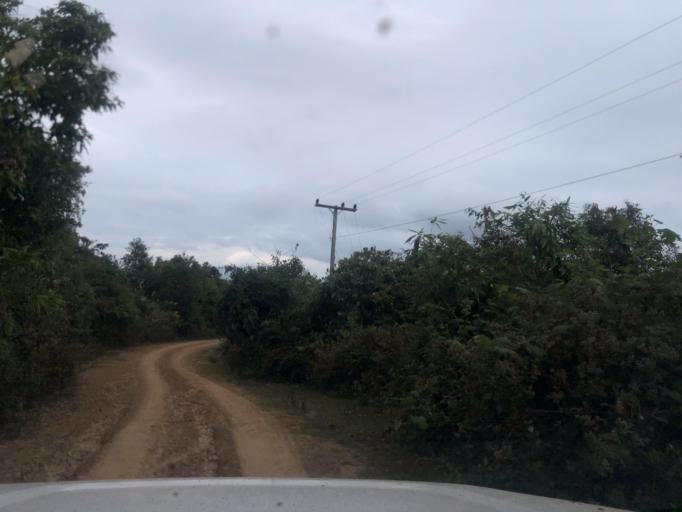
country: LA
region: Phongsali
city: Khoa
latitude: 21.2682
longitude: 102.5838
